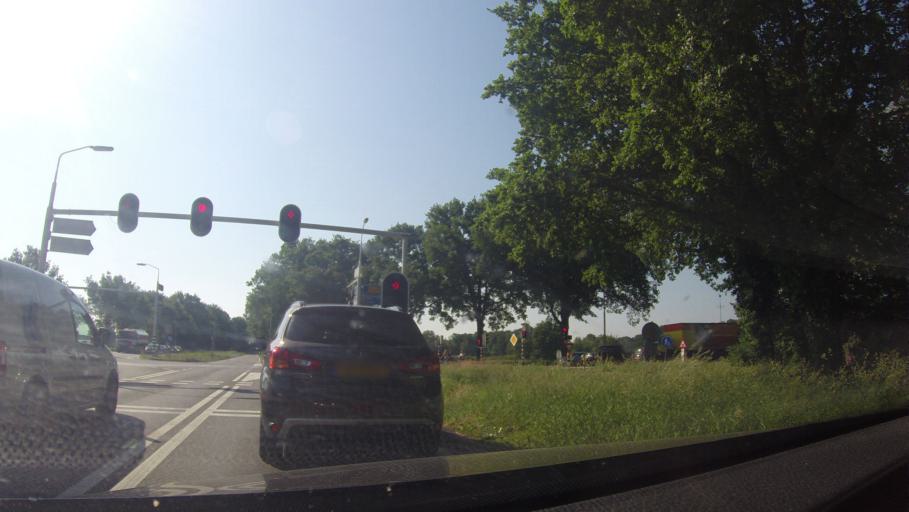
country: NL
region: Overijssel
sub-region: Gemeente Raalte
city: Raalte
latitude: 52.4003
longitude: 6.2679
